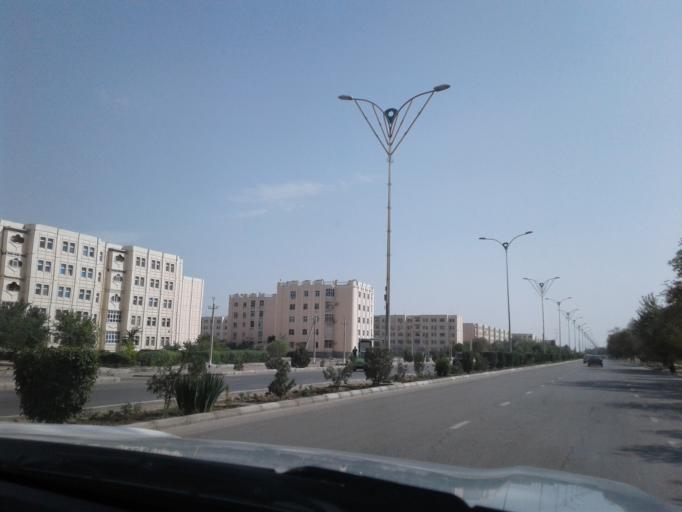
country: TM
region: Dasoguz
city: Dasoguz
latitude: 41.8429
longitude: 59.9305
